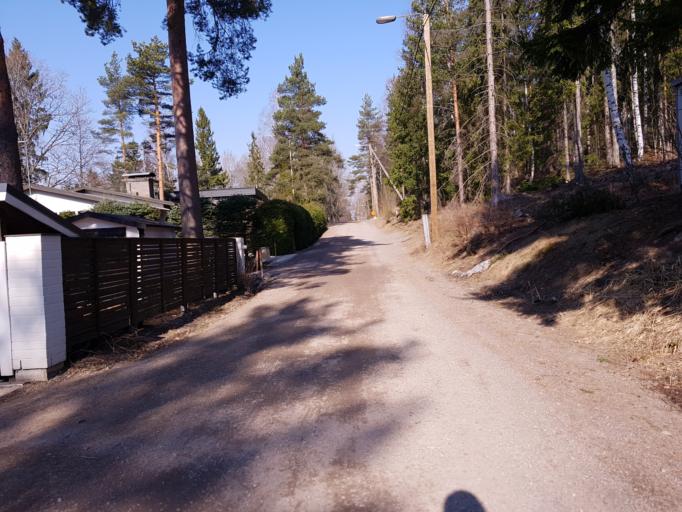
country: FI
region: Uusimaa
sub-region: Helsinki
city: Kilo
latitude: 60.2521
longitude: 24.7647
